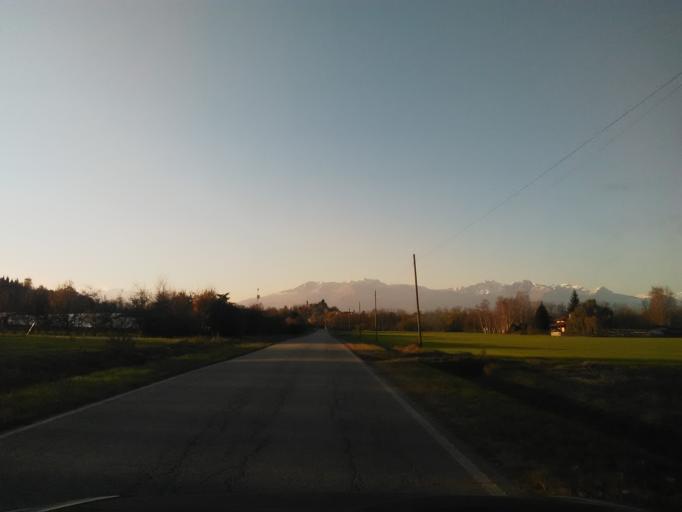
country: IT
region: Piedmont
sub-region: Provincia di Biella
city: Cerrione
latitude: 45.4617
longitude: 8.0784
